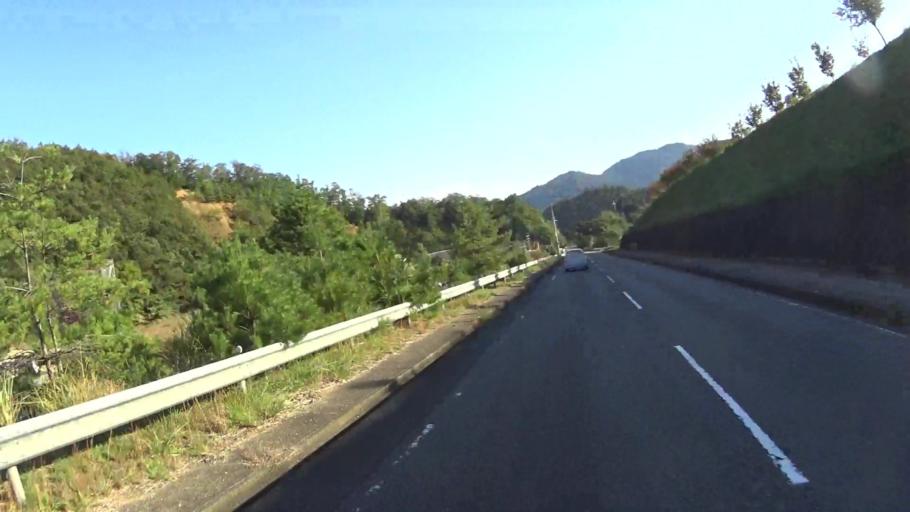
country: JP
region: Kyoto
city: Fukuchiyama
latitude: 35.3758
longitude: 135.0992
